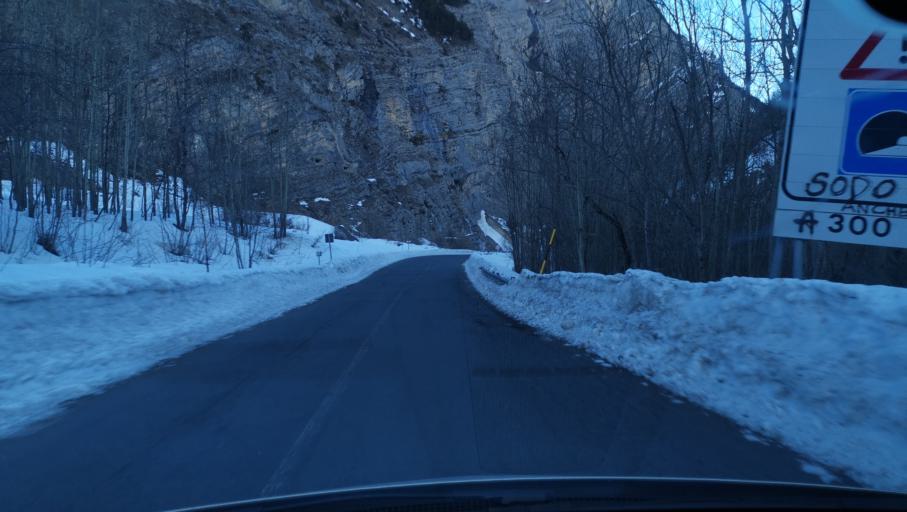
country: IT
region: Piedmont
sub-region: Provincia di Cuneo
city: Bersezio
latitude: 44.3585
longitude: 6.9980
